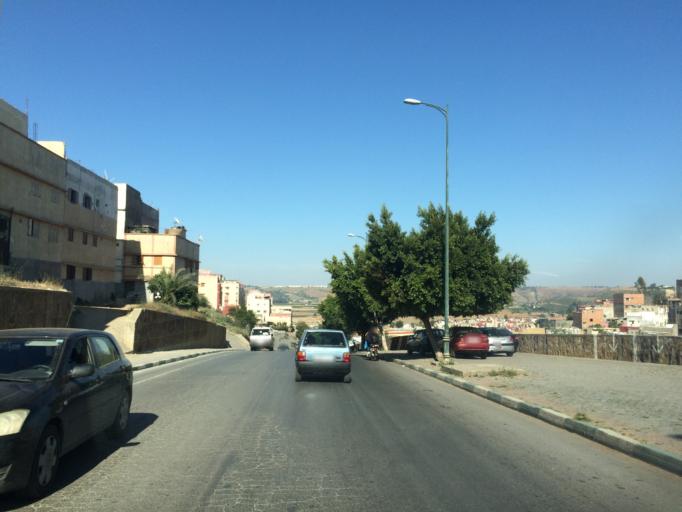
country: MA
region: Rabat-Sale-Zemmour-Zaer
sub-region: Rabat
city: Rabat
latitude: 33.9911
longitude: -6.8126
